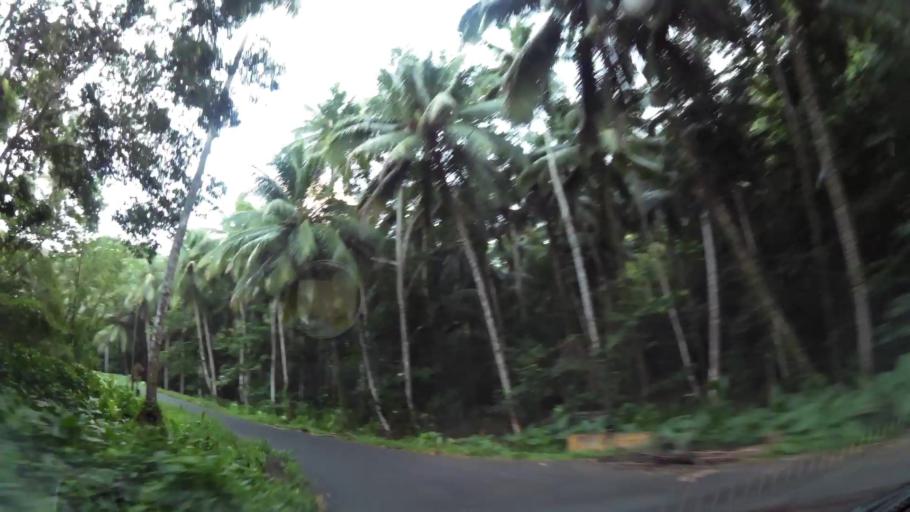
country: DM
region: Saint Andrew
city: Calibishie
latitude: 15.5907
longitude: -61.3619
